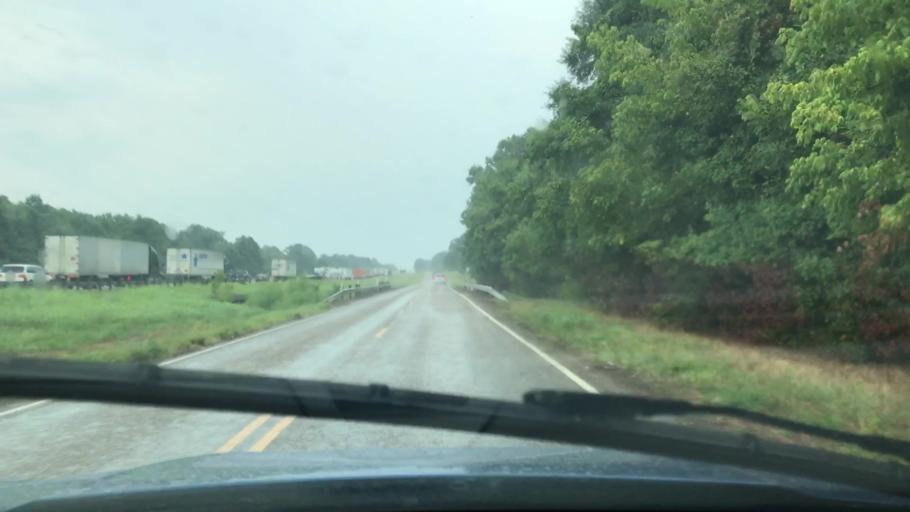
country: US
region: Texas
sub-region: Harrison County
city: Waskom
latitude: 32.4873
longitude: -94.1333
